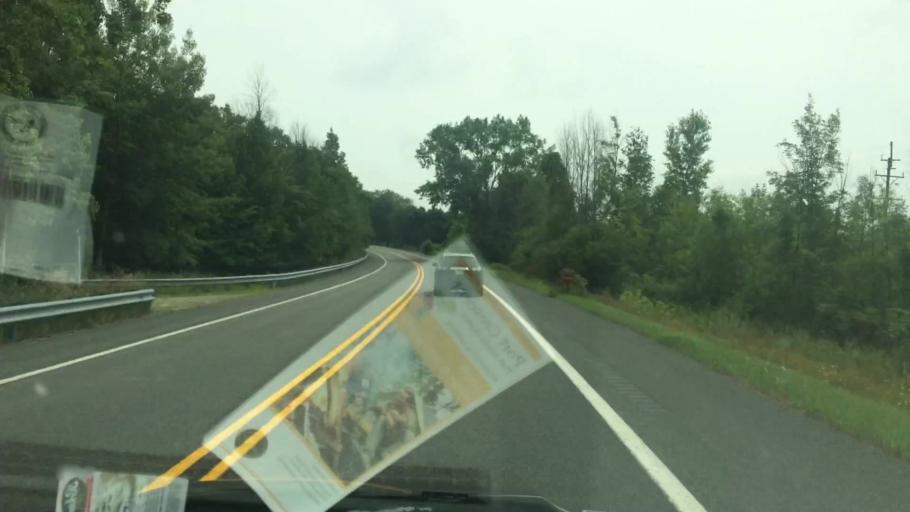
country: US
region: Michigan
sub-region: Huron County
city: Harbor Beach
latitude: 44.0220
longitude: -82.8149
